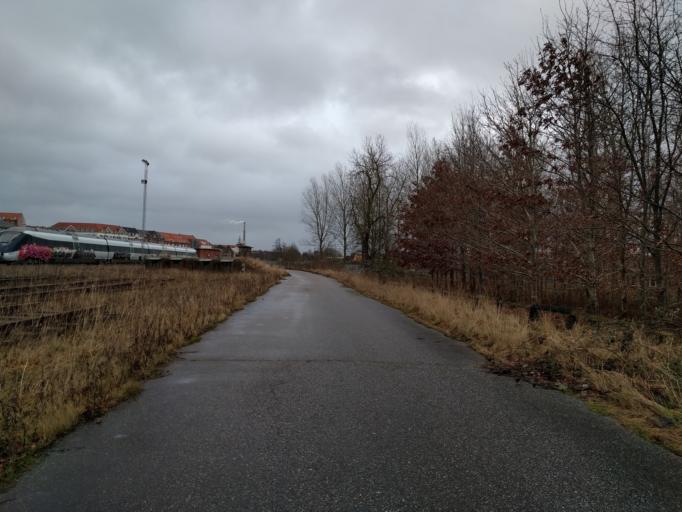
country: DK
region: Central Jutland
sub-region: Randers Kommune
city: Randers
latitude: 56.4612
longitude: 10.0208
